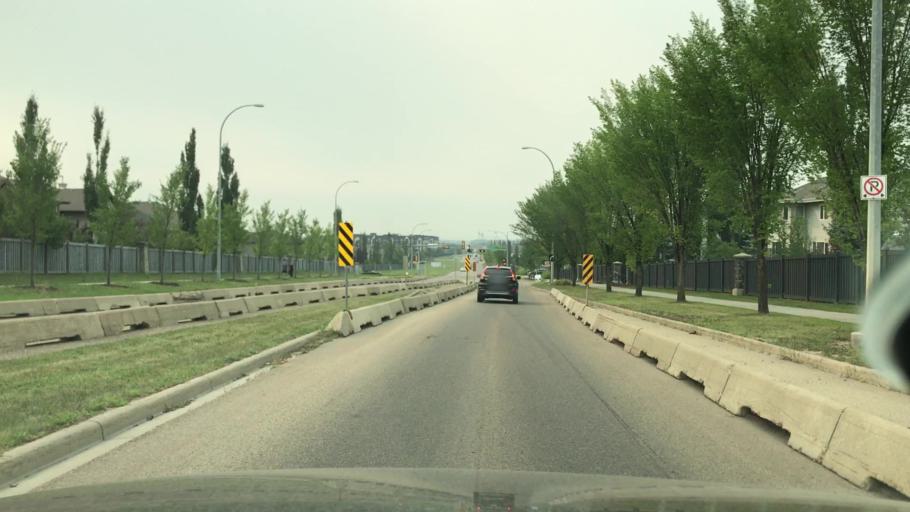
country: CA
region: Alberta
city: Edmonton
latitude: 53.4464
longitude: -113.5657
